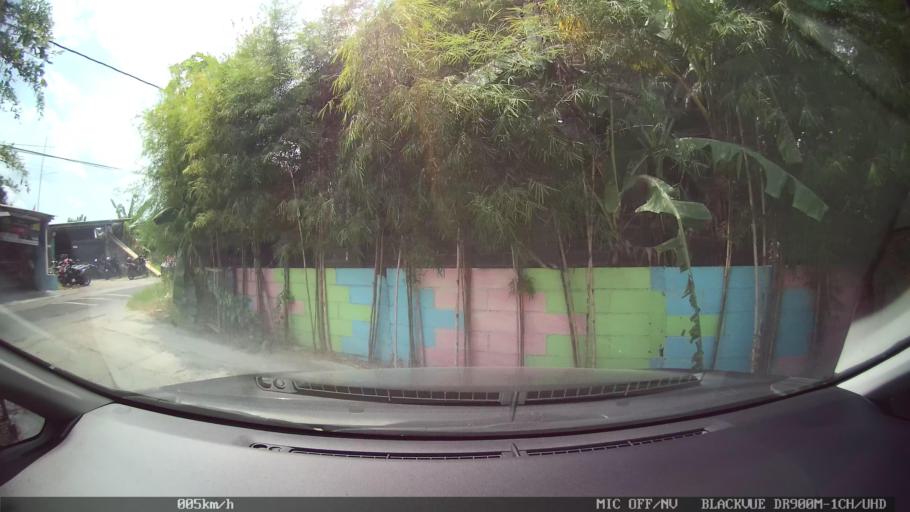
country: ID
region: Daerah Istimewa Yogyakarta
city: Kasihan
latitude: -7.8164
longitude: 110.3432
